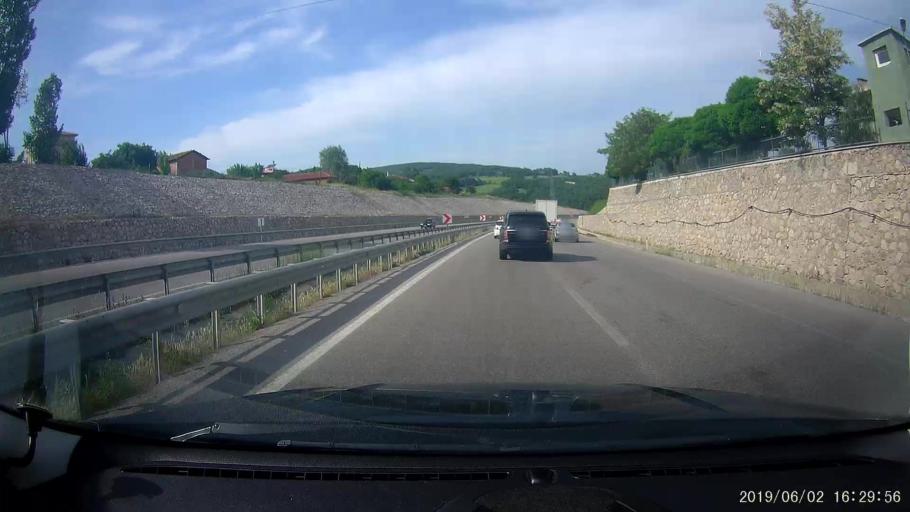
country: TR
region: Samsun
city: Ladik
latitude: 41.0201
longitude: 35.8735
